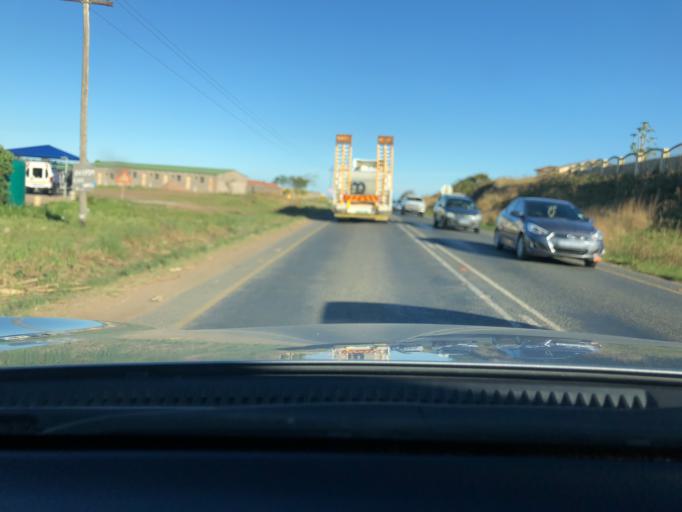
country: ZA
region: KwaZulu-Natal
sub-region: eThekwini Metropolitan Municipality
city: Umkomaas
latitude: -30.0084
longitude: 30.8037
